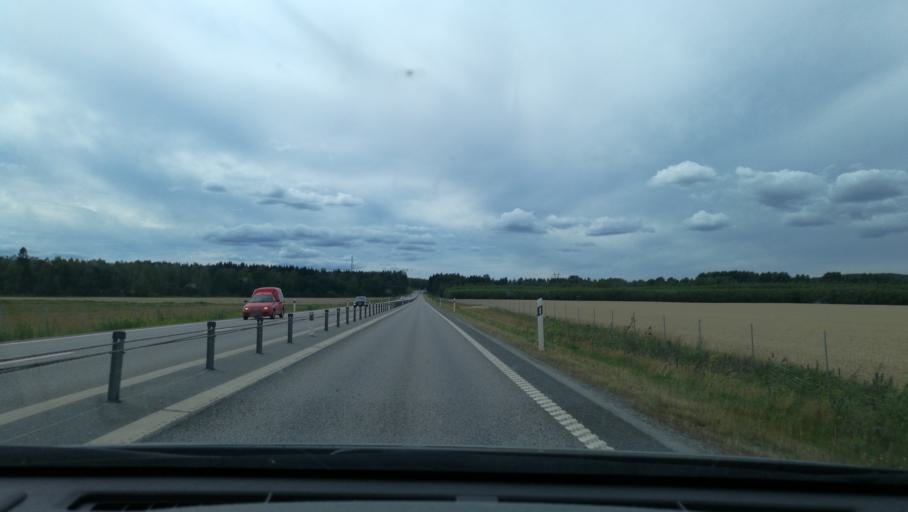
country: SE
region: OEstergoetland
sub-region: Norrkopings Kommun
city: Jursla
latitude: 58.6336
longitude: 16.1240
